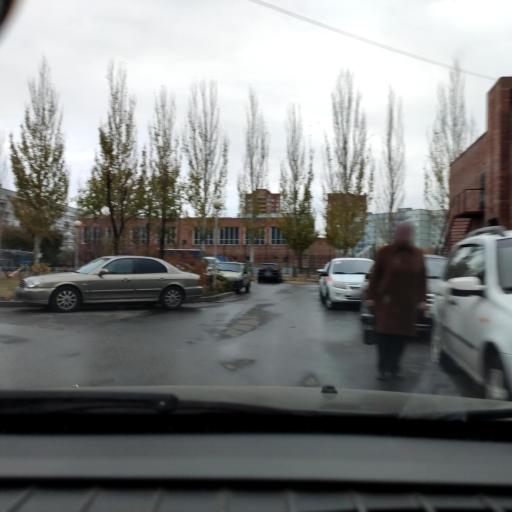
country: RU
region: Samara
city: Tol'yatti
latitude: 53.5446
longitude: 49.3324
